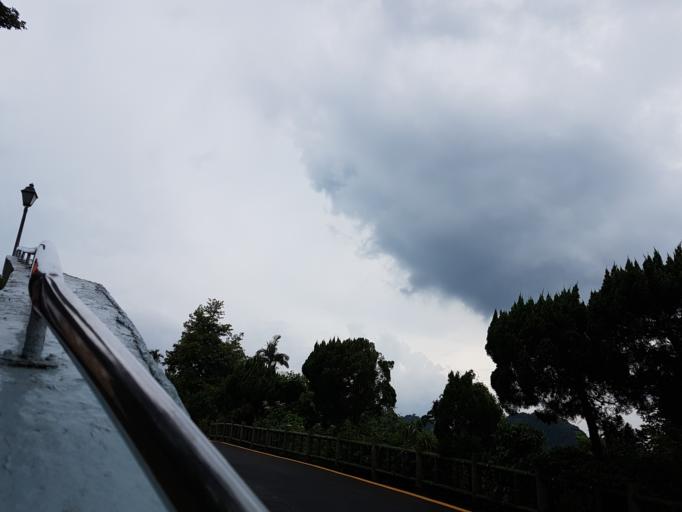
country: TW
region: Taiwan
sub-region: Keelung
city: Keelung
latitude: 25.0531
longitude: 121.6629
